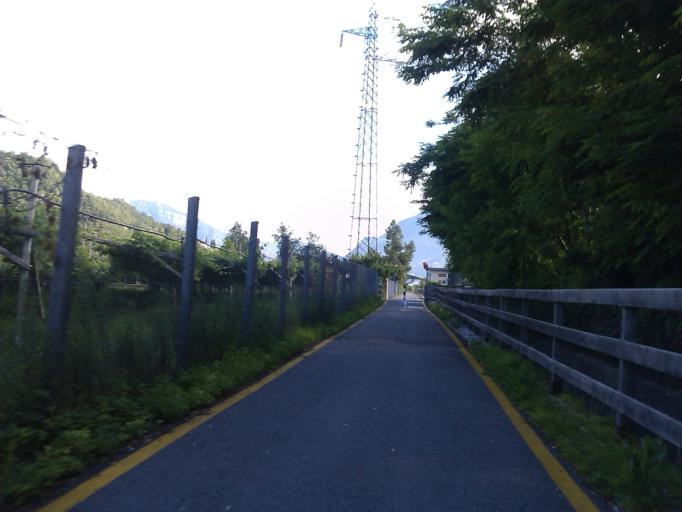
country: IT
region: Trentino-Alto Adige
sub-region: Provincia di Trento
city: Meano
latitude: 46.1214
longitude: 11.1087
